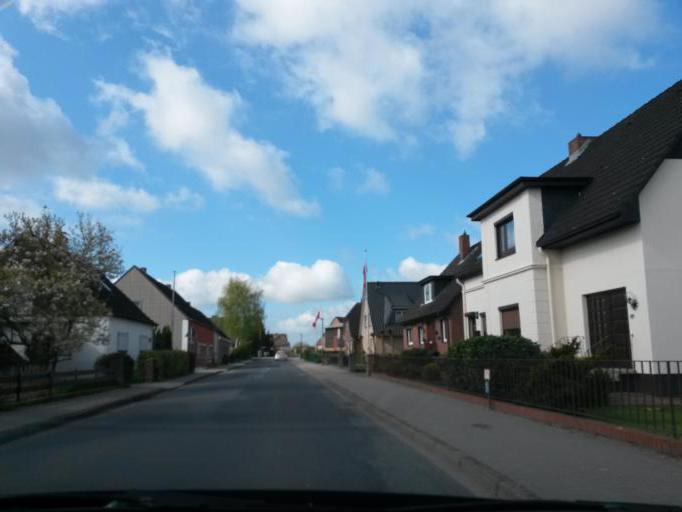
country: DE
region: Schleswig-Holstein
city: Hetlingen
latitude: 53.6081
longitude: 9.6391
